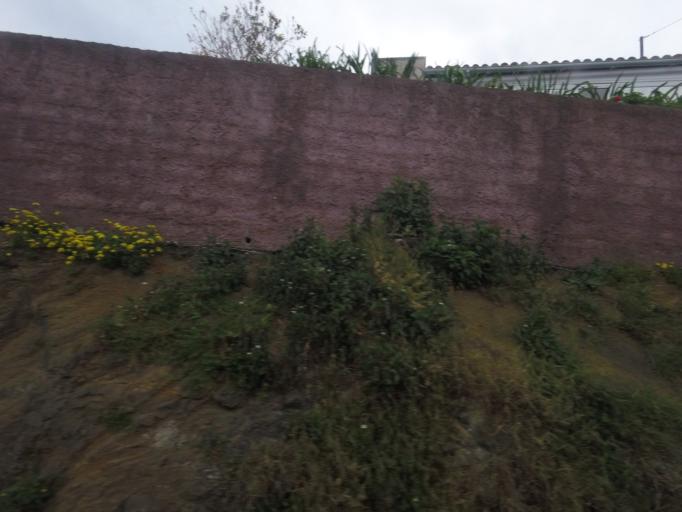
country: PT
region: Madeira
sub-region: Santana
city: Santana
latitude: 32.7649
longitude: -16.8154
